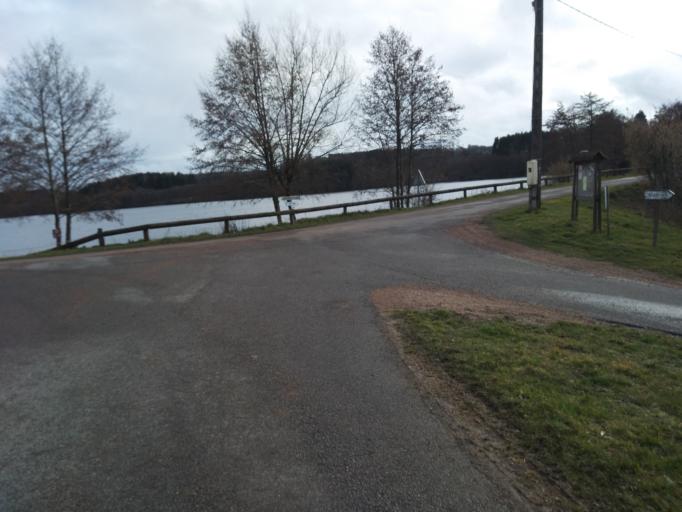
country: FR
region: Bourgogne
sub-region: Departement de la Cote-d'Or
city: Saulieu
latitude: 47.2761
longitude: 4.1439
